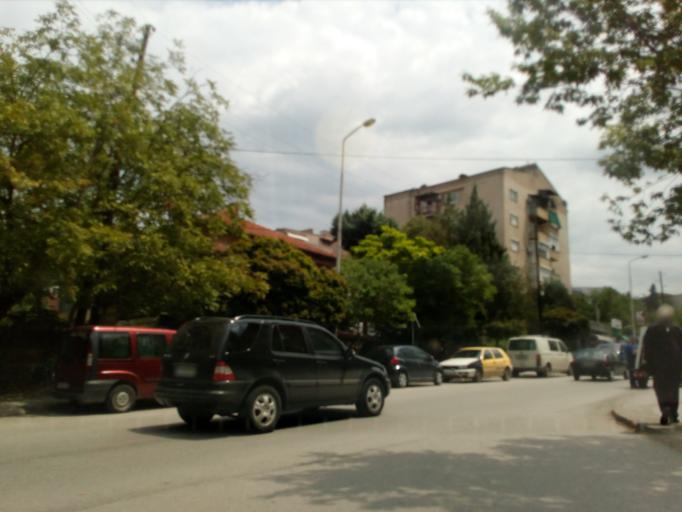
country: MK
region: Veles
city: Veles
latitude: 41.7154
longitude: 21.7668
